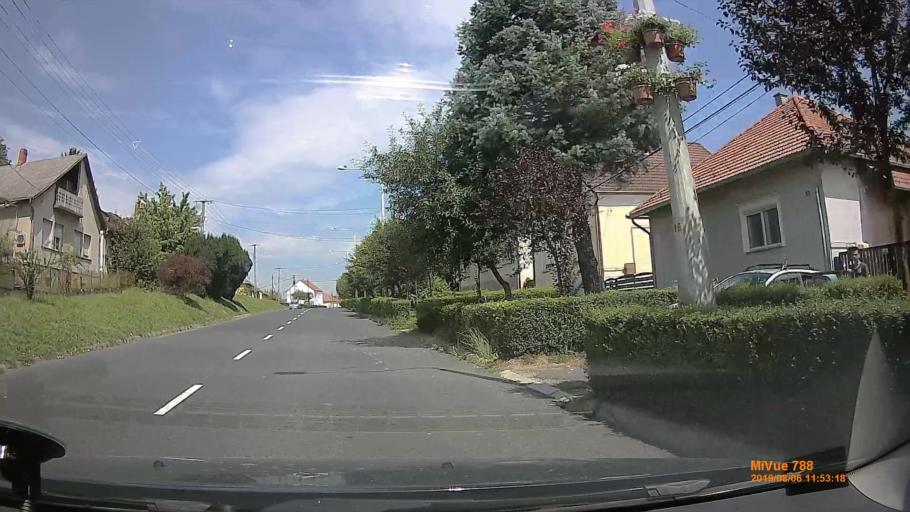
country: HU
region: Zala
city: Letenye
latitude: 46.4279
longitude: 16.7223
